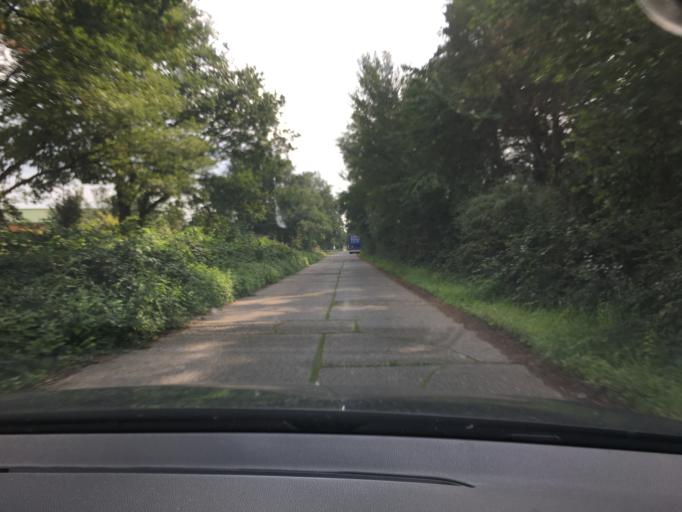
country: DE
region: North Rhine-Westphalia
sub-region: Regierungsbezirk Koln
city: Kreuzau
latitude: 50.7633
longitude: 6.5168
